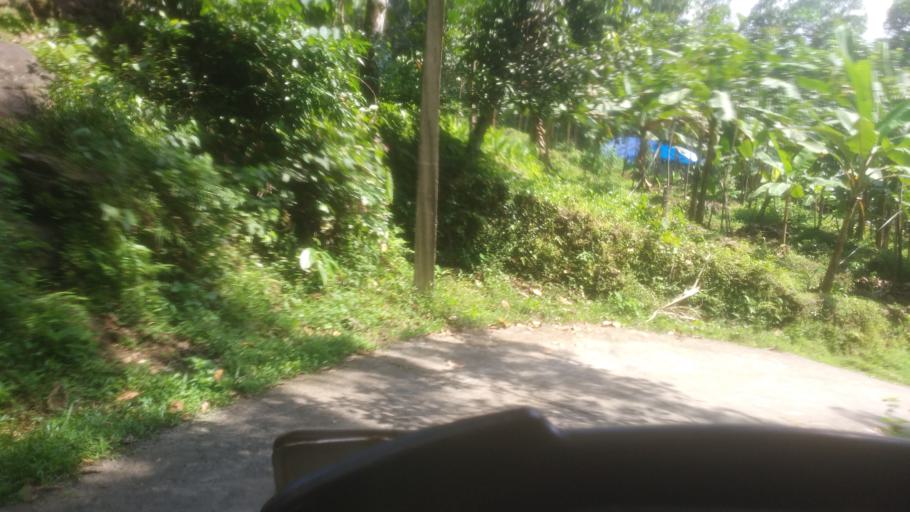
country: IN
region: Kerala
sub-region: Idukki
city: Idukki
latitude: 9.9618
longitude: 76.8251
